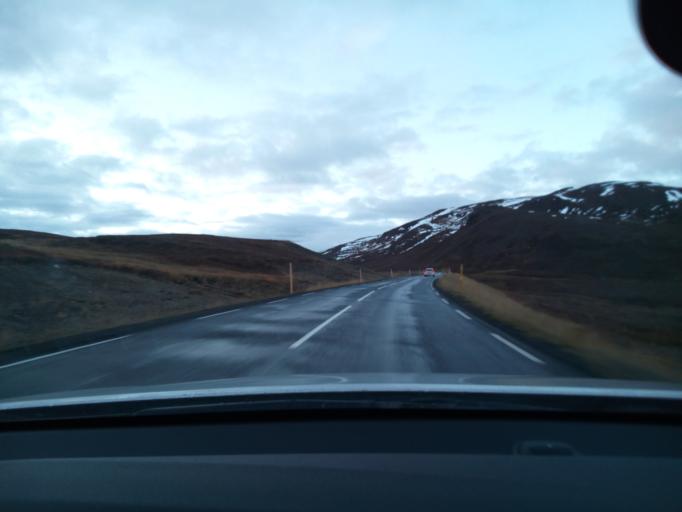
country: IS
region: Northeast
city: Akureyri
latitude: 65.7998
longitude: -17.9494
